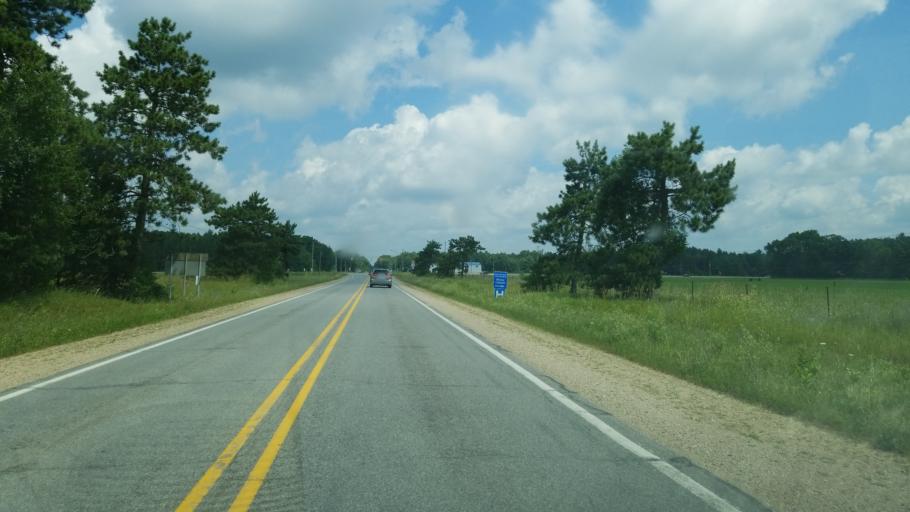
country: US
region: Michigan
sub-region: Montcalm County
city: Howard City
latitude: 43.4284
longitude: -85.4612
